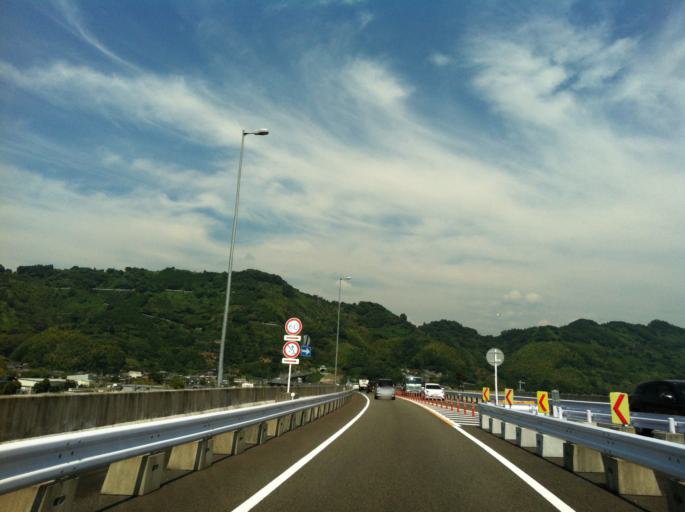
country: JP
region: Shizuoka
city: Shizuoka-shi
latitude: 35.0168
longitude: 138.3950
